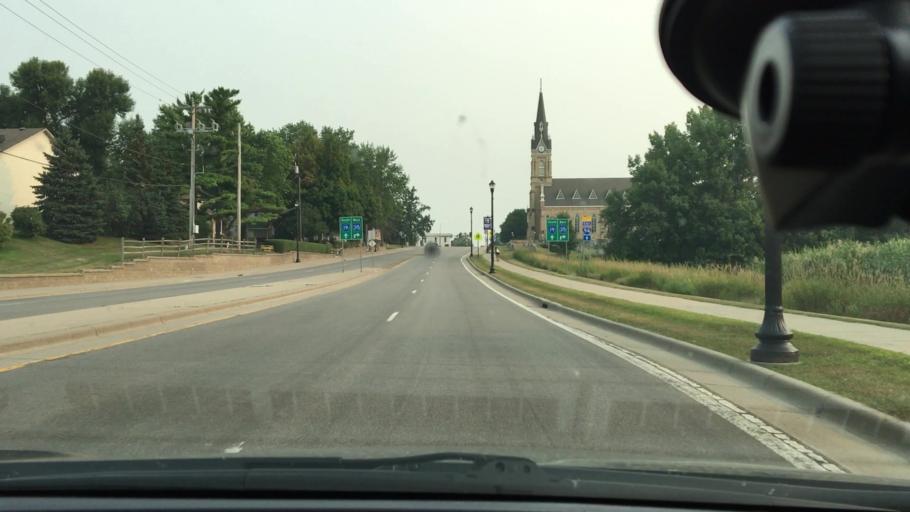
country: US
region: Minnesota
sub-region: Wright County
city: Saint Michael
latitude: 45.2132
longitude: -93.6649
